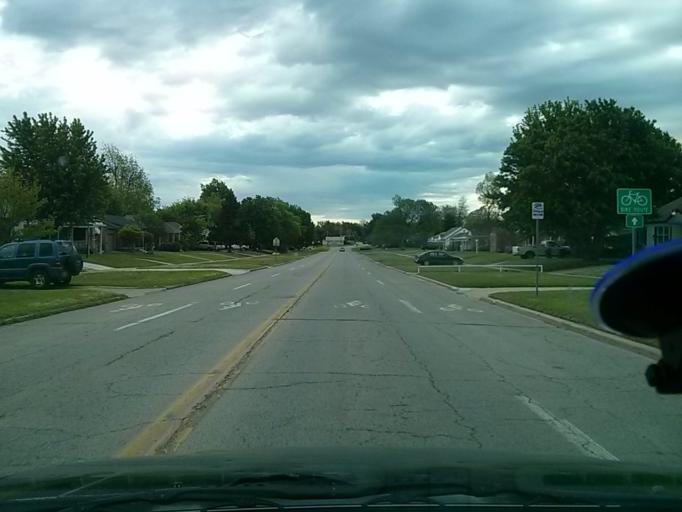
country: US
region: Oklahoma
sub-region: Tulsa County
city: Tulsa
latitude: 36.1566
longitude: -95.9537
